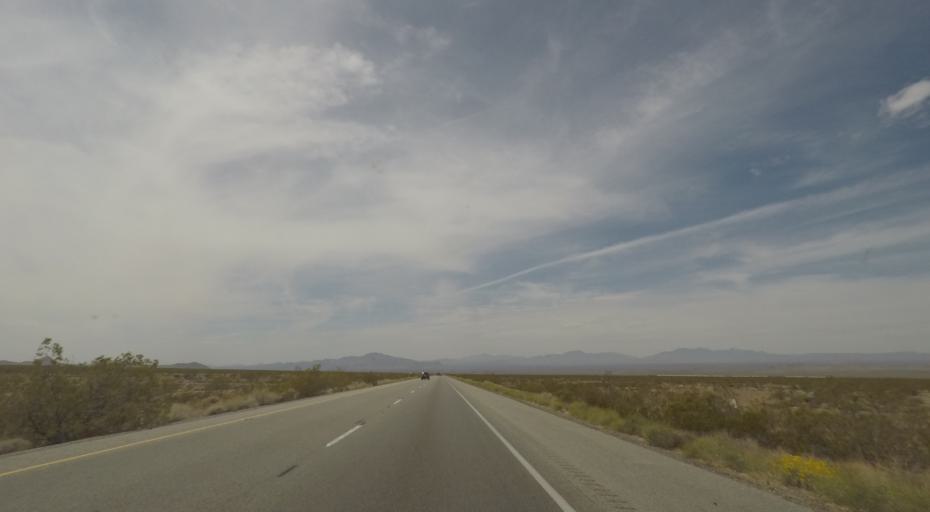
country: US
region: California
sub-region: San Bernardino County
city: Needles
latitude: 34.8264
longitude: -115.0788
